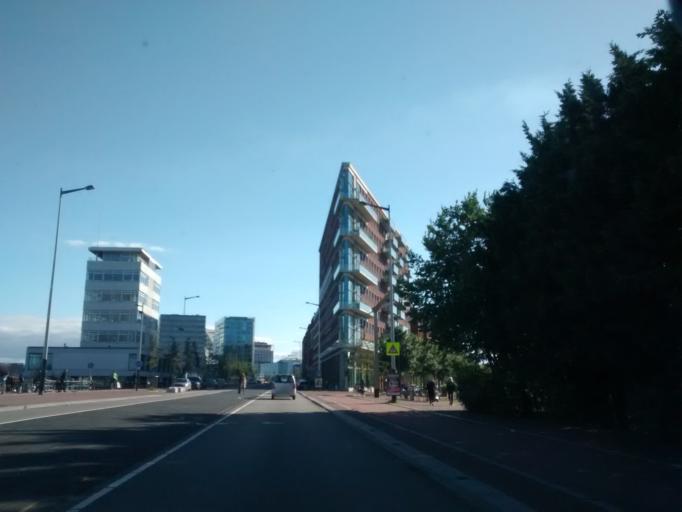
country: NL
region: North Holland
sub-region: Gemeente Amsterdam
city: Amsterdam
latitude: 52.3886
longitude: 4.8918
